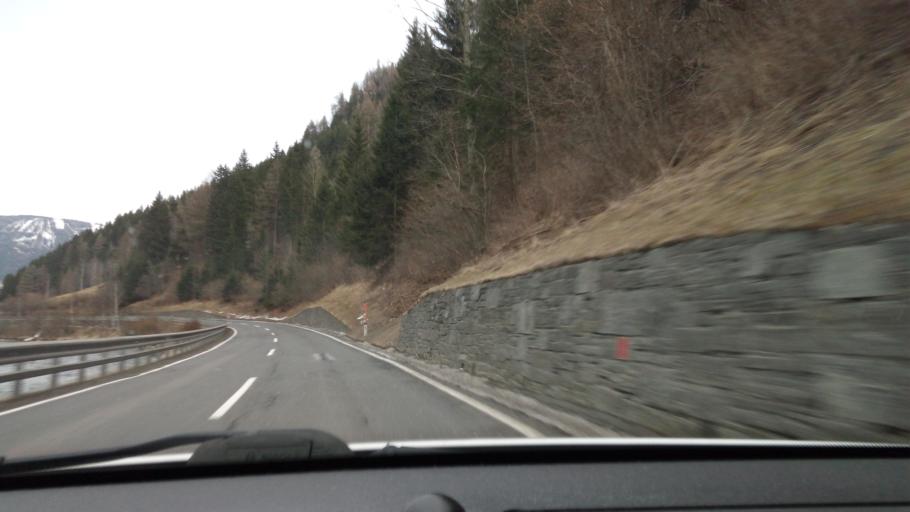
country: AT
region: Salzburg
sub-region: Politischer Bezirk Tamsweg
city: Ramingstein
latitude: 47.0738
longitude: 13.8532
